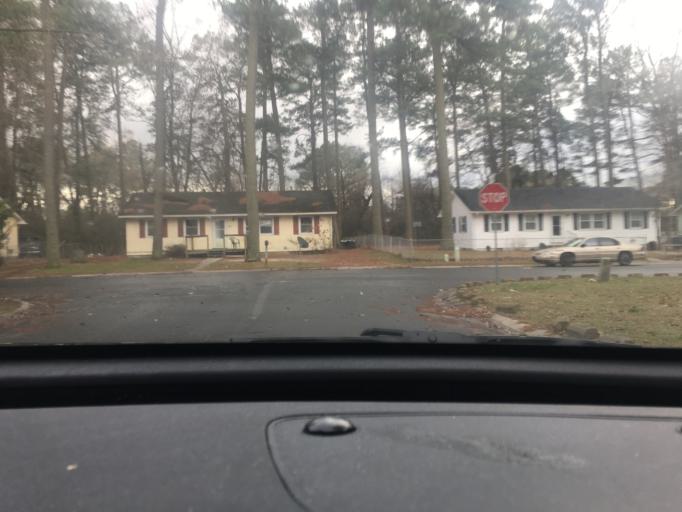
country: US
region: Maryland
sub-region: Wicomico County
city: Salisbury
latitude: 38.3796
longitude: -75.6134
